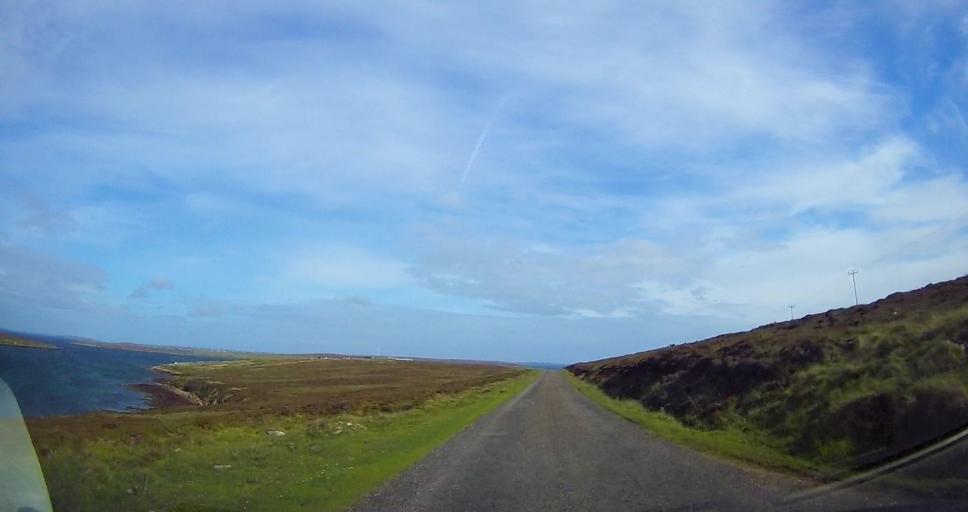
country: GB
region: Scotland
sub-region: Orkney Islands
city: Stromness
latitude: 58.8576
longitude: -3.2152
